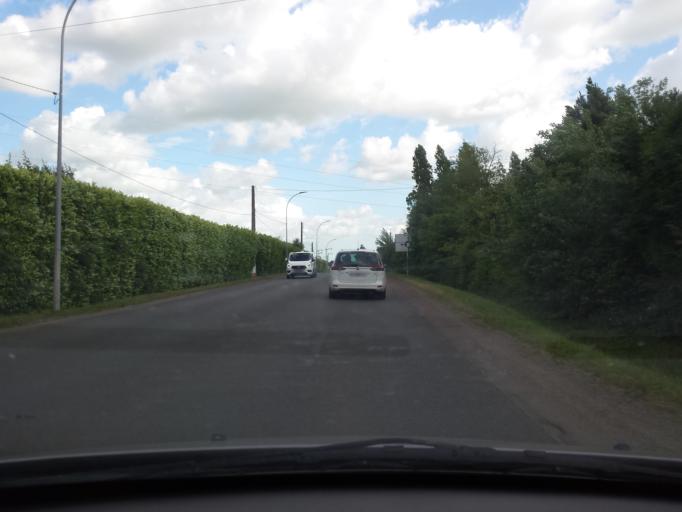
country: FR
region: Pays de la Loire
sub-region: Departement de la Vendee
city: Lucon
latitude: 46.4693
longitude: -1.1754
